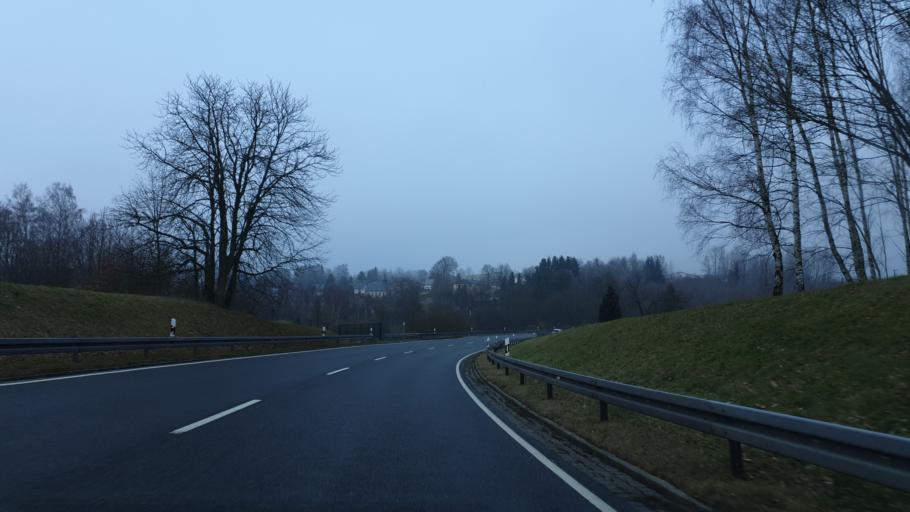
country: DE
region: Saxony
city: Bad Brambach
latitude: 50.2186
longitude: 12.3184
